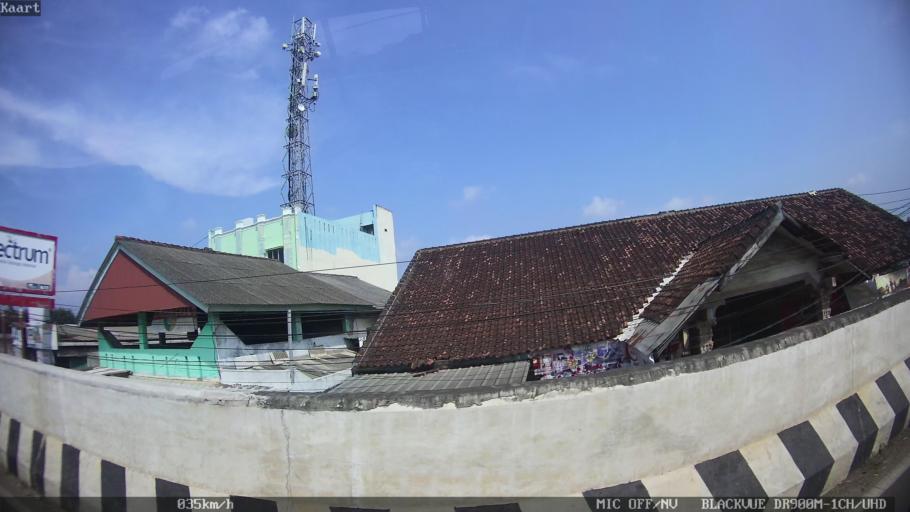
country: ID
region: Lampung
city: Kedaton
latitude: -5.3604
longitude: 105.2577
